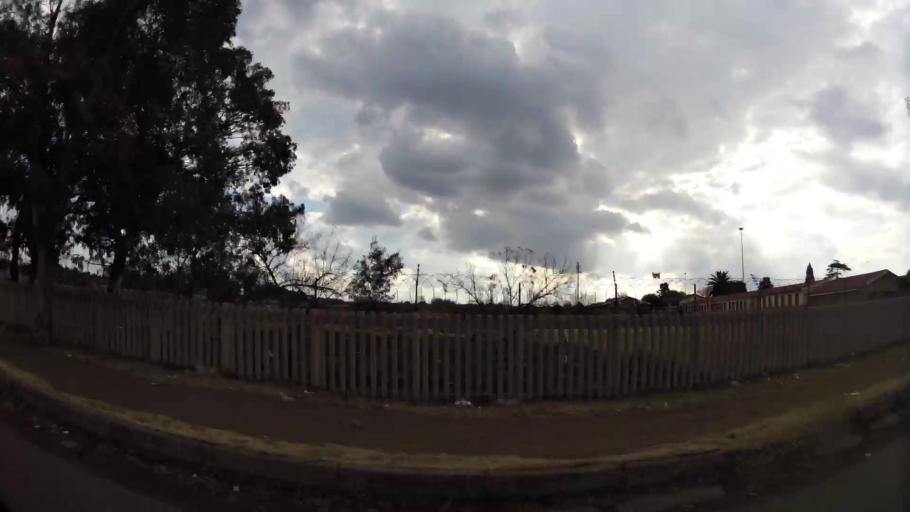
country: ZA
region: Gauteng
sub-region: Sedibeng District Municipality
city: Vanderbijlpark
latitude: -26.6692
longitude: 27.8492
